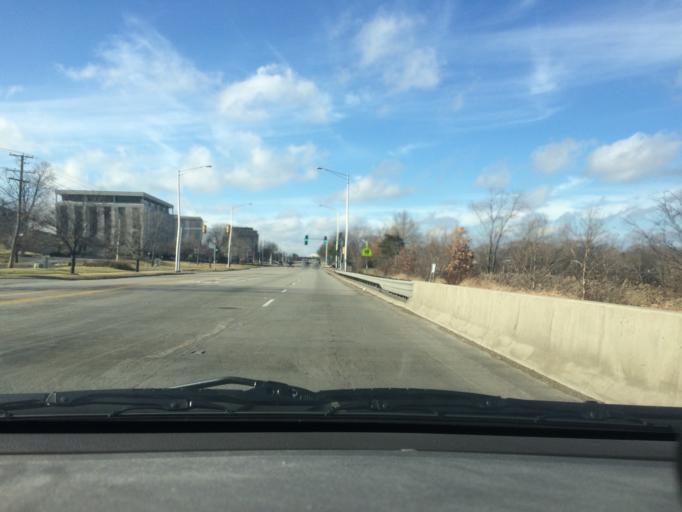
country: US
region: Illinois
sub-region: Cook County
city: Rolling Meadows
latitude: 42.0604
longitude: -88.0170
